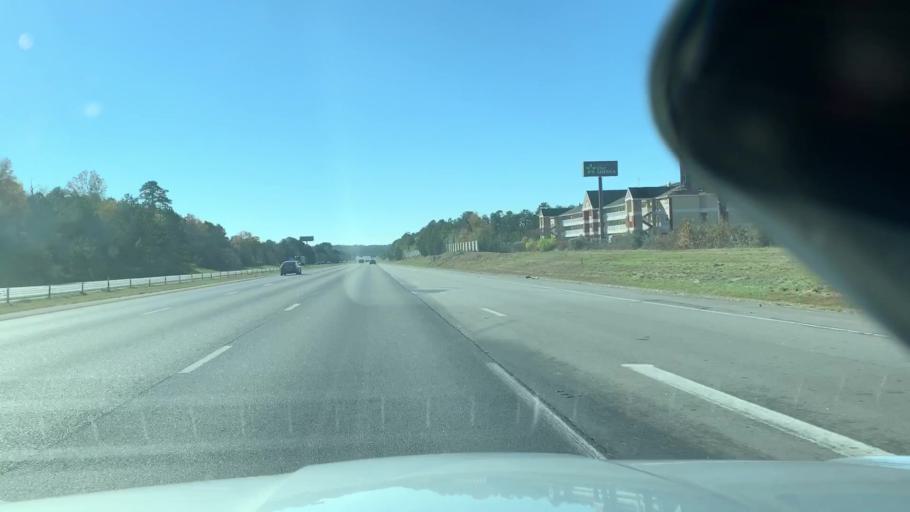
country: US
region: South Carolina
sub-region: Richland County
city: Forest Acres
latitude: 34.0182
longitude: -80.9487
